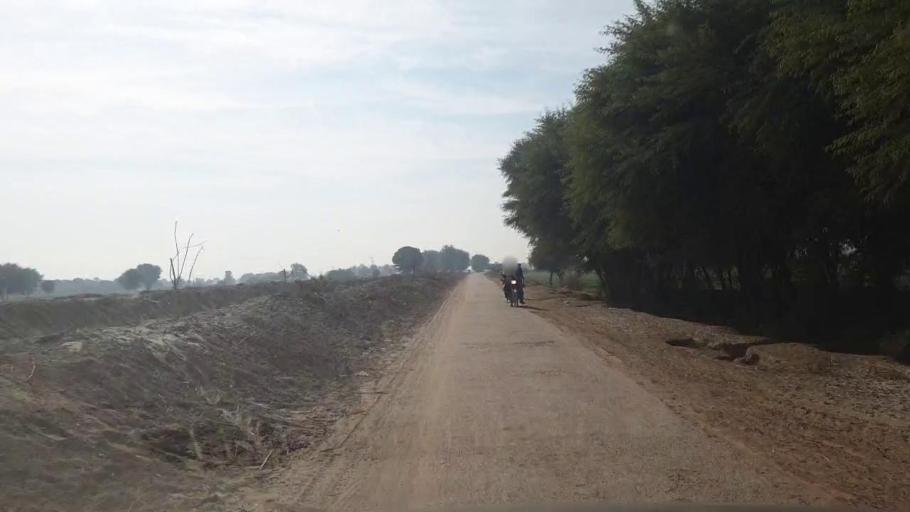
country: PK
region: Sindh
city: Shahpur Chakar
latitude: 26.1872
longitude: 68.5834
